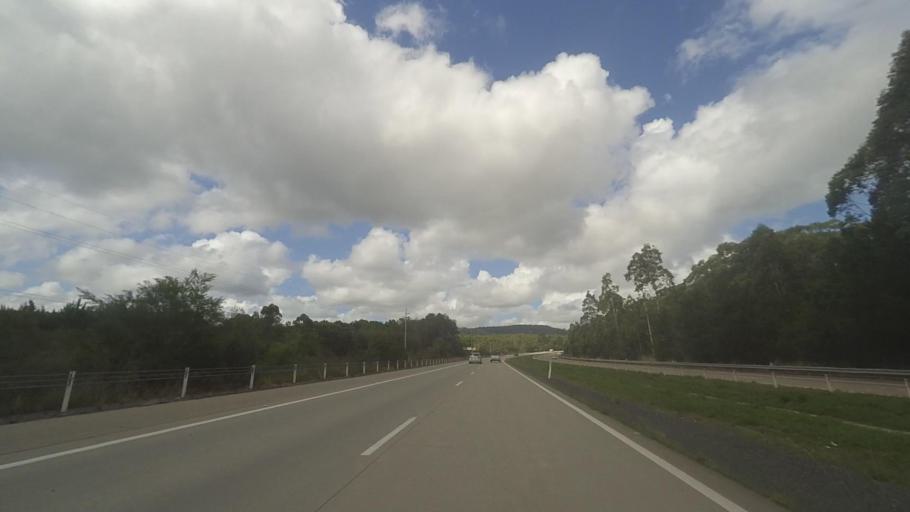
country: AU
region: New South Wales
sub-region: Great Lakes
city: Bulahdelah
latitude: -32.3881
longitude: 152.2257
